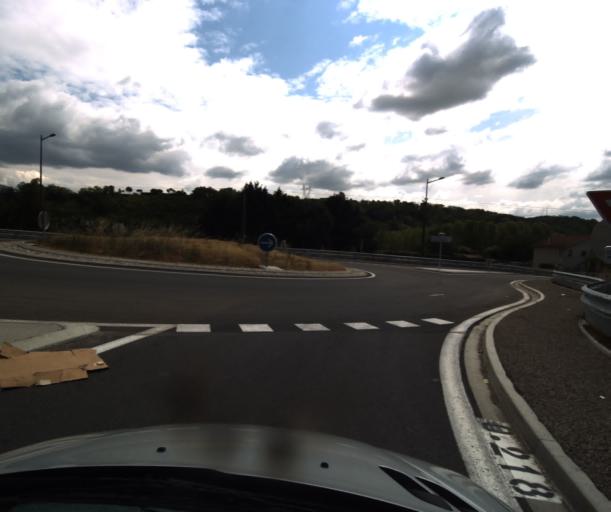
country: FR
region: Midi-Pyrenees
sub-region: Departement du Tarn-et-Garonne
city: Montauban
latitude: 43.9926
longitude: 1.3503
